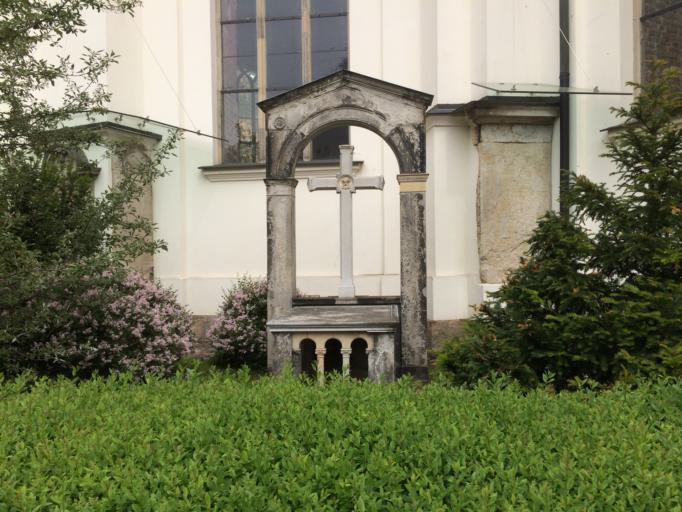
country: DE
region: Berlin
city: Berlin
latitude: 52.5168
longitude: 13.4128
